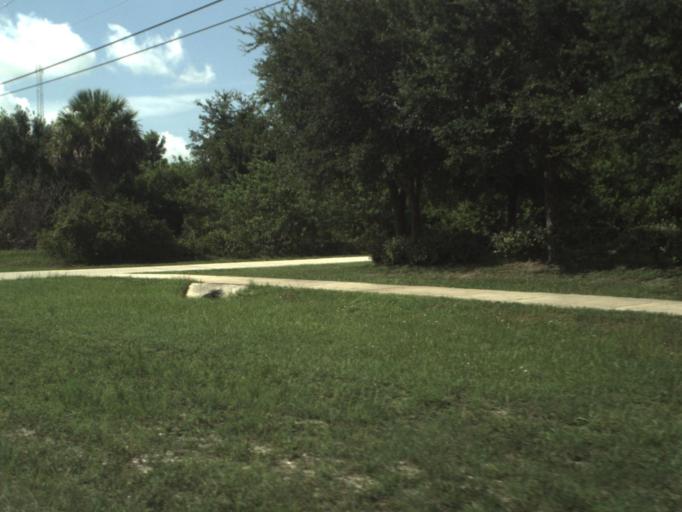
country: US
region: Florida
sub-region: Saint Lucie County
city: Port Saint Lucie
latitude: 27.2308
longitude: -80.3755
